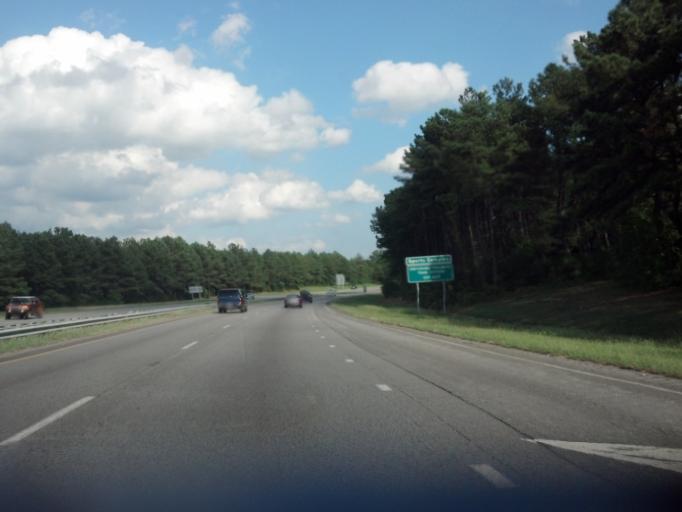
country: US
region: North Carolina
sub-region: Nash County
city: Rocky Mount
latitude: 35.9643
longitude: -77.8037
